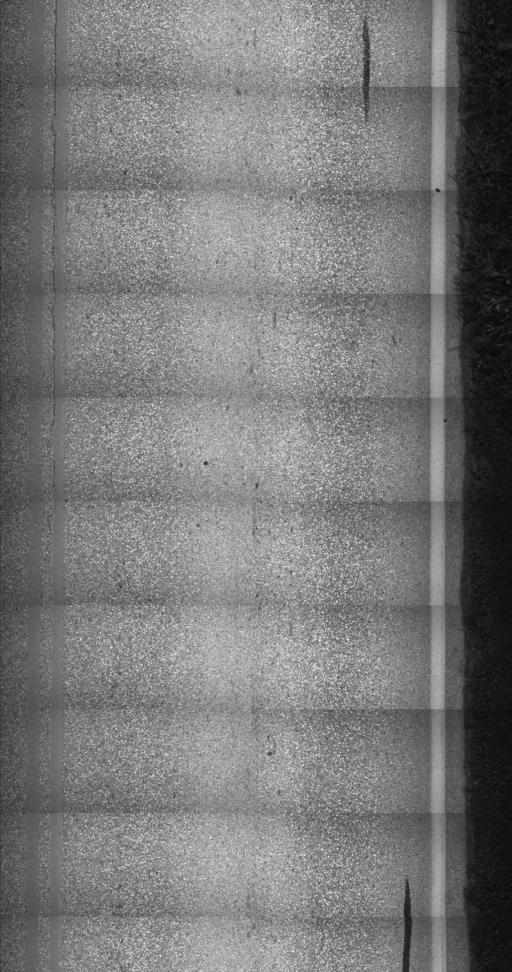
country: US
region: New York
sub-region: Washington County
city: Granville
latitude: 43.3482
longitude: -73.1714
